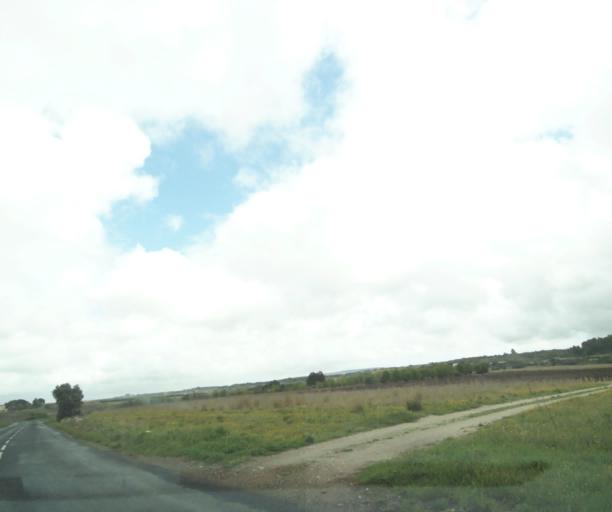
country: FR
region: Languedoc-Roussillon
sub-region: Departement de l'Herault
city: Montbazin
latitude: 43.5289
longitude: 3.6938
